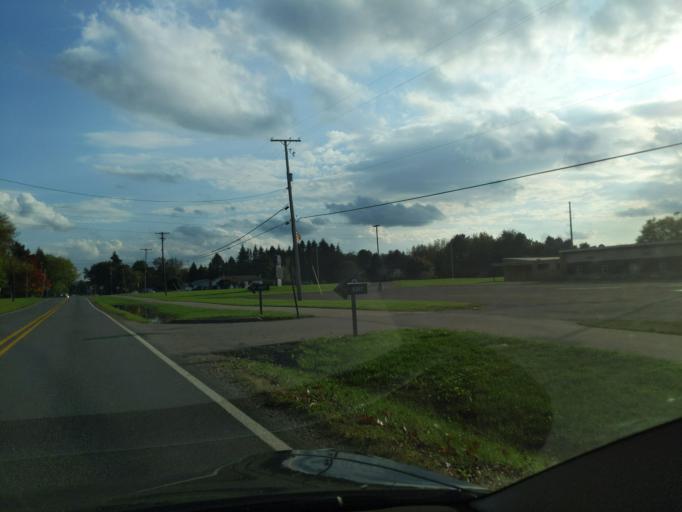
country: US
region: Michigan
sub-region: Jackson County
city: Jackson
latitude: 42.3288
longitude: -84.4629
